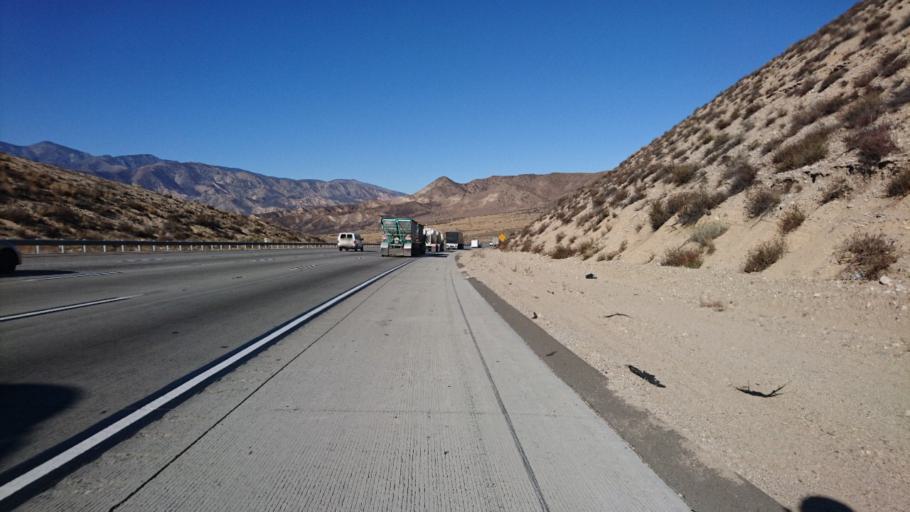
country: US
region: California
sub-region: San Bernardino County
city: Oak Hills
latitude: 34.3447
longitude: -117.4630
